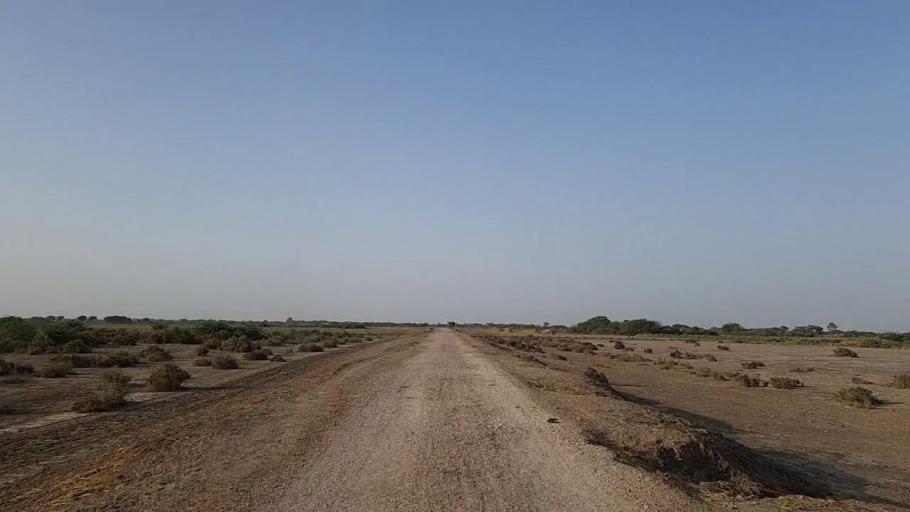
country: PK
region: Sindh
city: Jati
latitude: 24.3765
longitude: 68.1478
